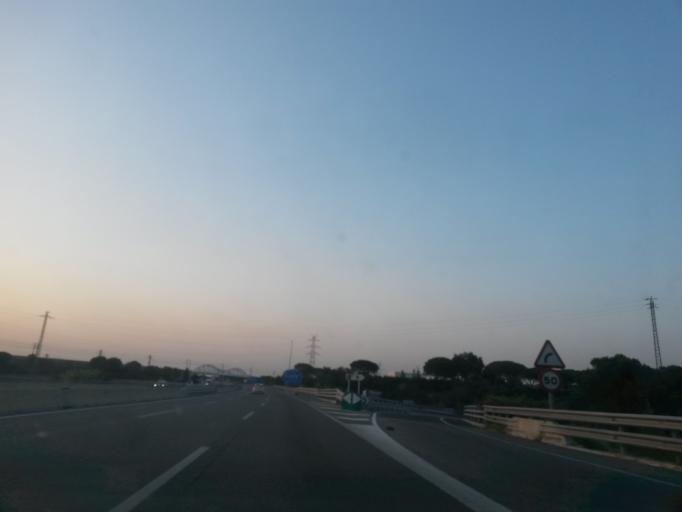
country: ES
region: Catalonia
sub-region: Provincia de Girona
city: Vilobi d'Onyar
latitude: 41.8947
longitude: 2.7752
